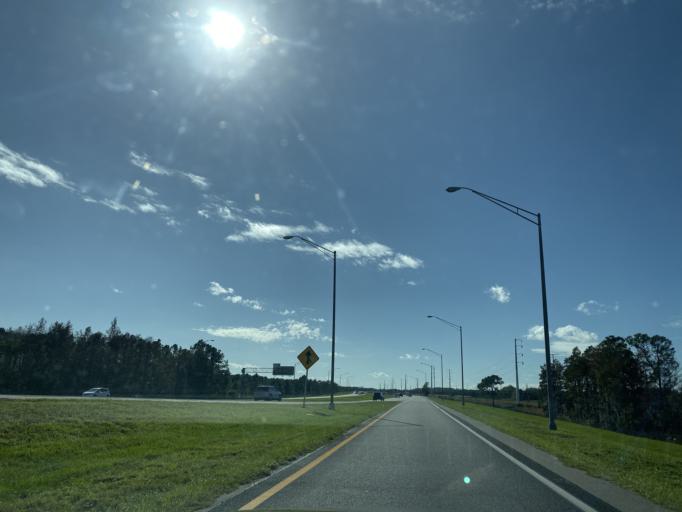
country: US
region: Florida
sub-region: Orange County
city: Meadow Woods
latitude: 28.3988
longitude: -81.2484
